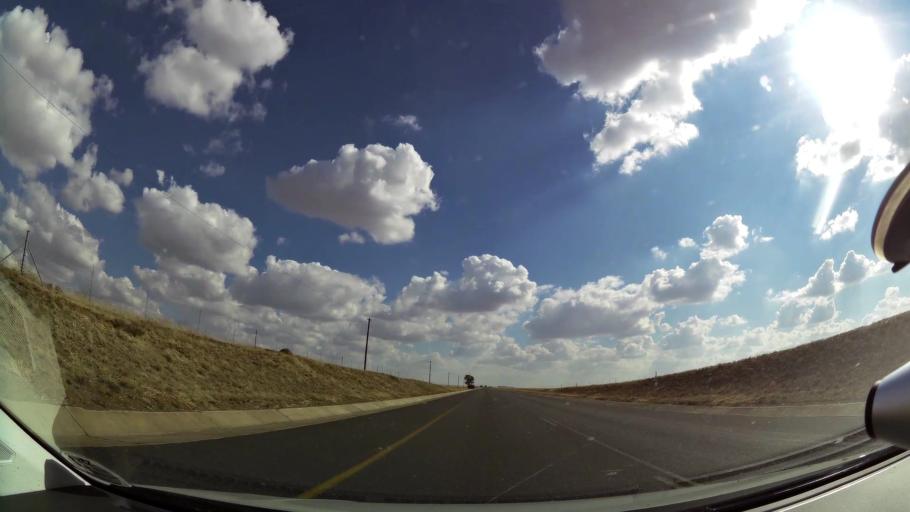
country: ZA
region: Orange Free State
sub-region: Mangaung Metropolitan Municipality
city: Bloemfontein
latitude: -29.1562
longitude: 25.7384
